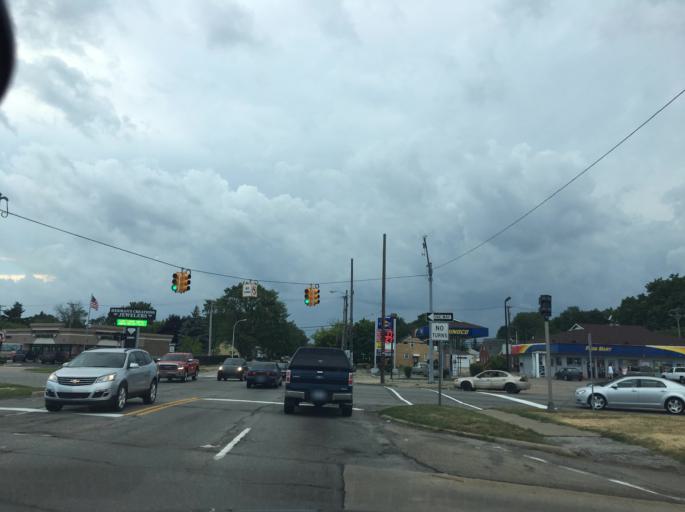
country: US
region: Michigan
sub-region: Macomb County
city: Roseville
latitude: 42.5099
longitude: -82.9281
